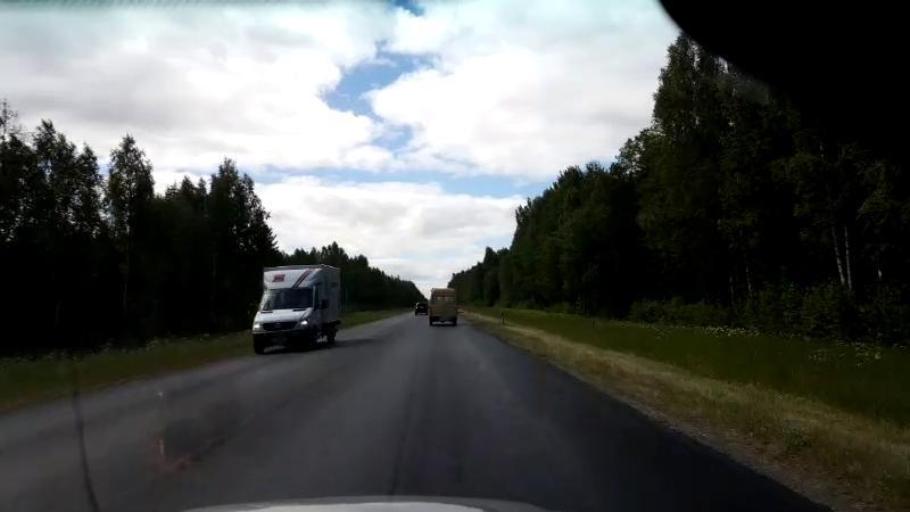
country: LV
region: Salacgrivas
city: Ainazi
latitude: 57.9576
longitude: 24.4415
